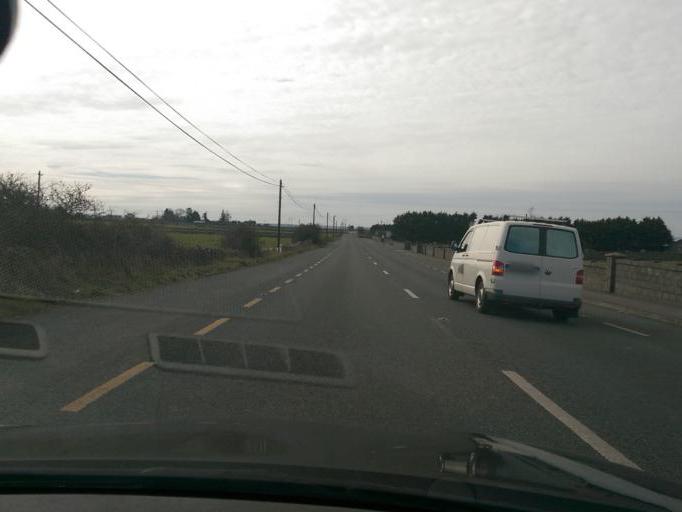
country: IE
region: Connaught
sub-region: County Galway
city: Claregalway
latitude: 53.3668
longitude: -8.9012
